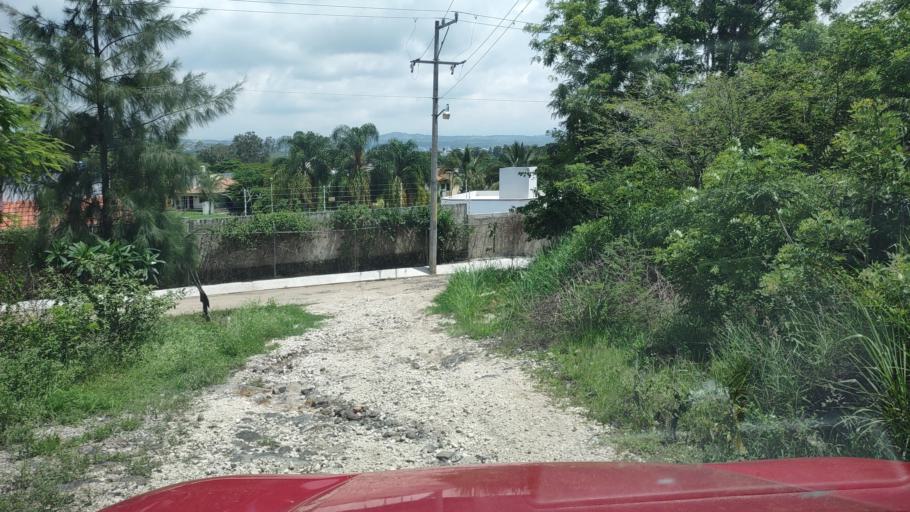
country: MX
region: Veracruz
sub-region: Emiliano Zapata
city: Dos Rios
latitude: 19.4626
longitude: -96.7893
